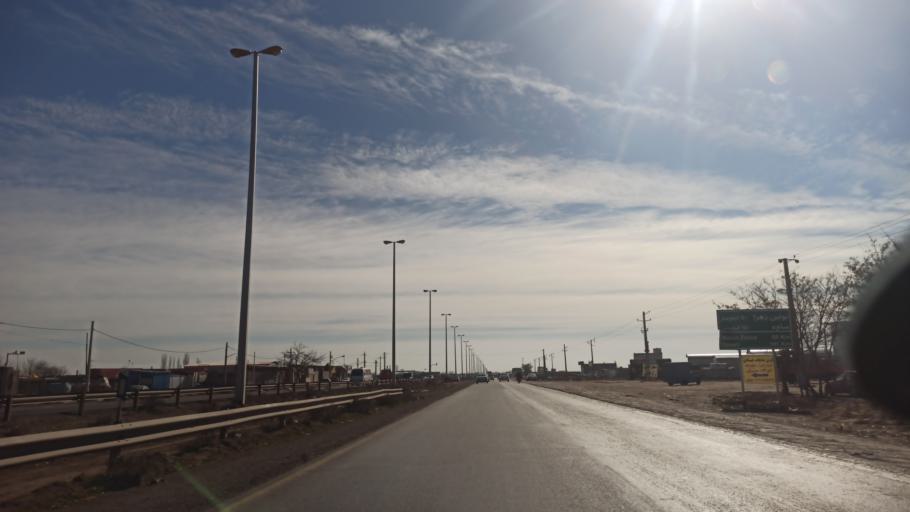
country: IR
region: Qazvin
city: Alvand
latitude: 36.2069
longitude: 50.0131
